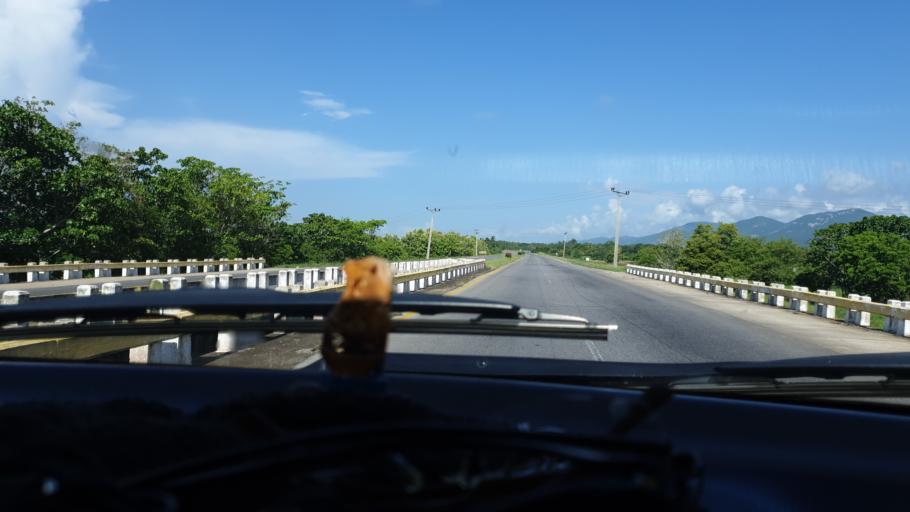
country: CU
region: Artemisa
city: San Cristobal
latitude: 22.7219
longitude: -83.0425
